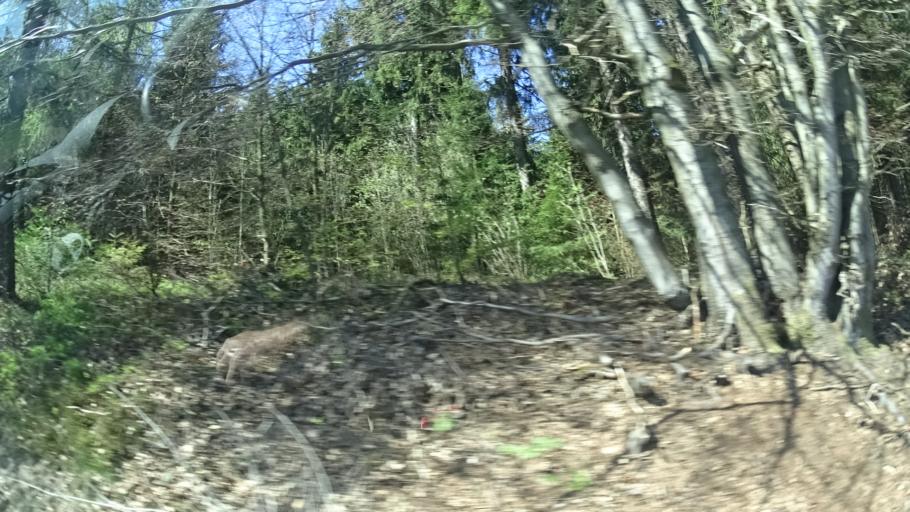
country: DE
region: Thuringia
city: Frauenwald
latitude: 50.5384
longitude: 10.8574
